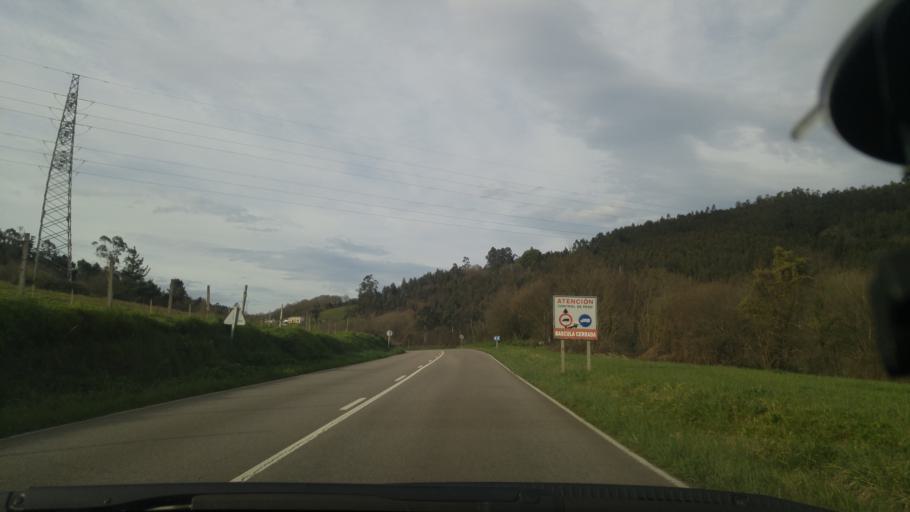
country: ES
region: Asturias
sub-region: Province of Asturias
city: Llanera
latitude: 43.4482
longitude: -5.8551
